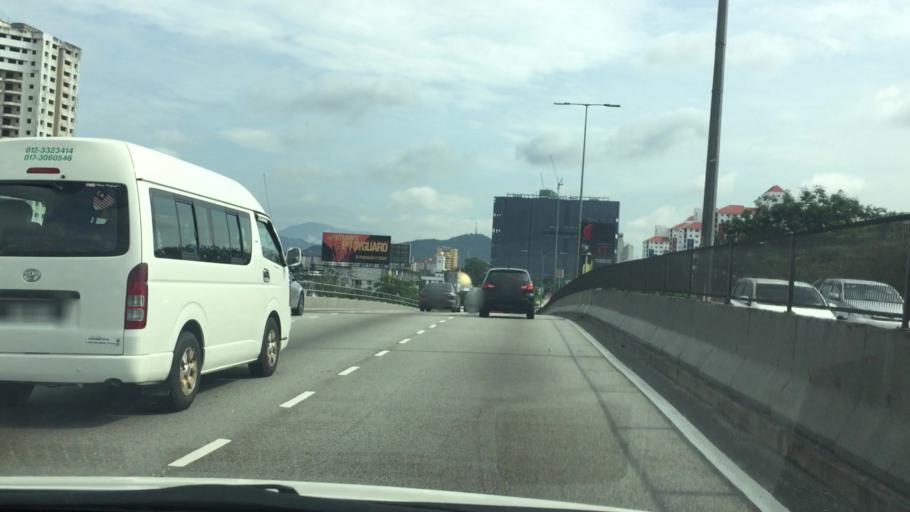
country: MY
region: Kuala Lumpur
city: Kuala Lumpur
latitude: 3.1462
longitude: 101.7441
